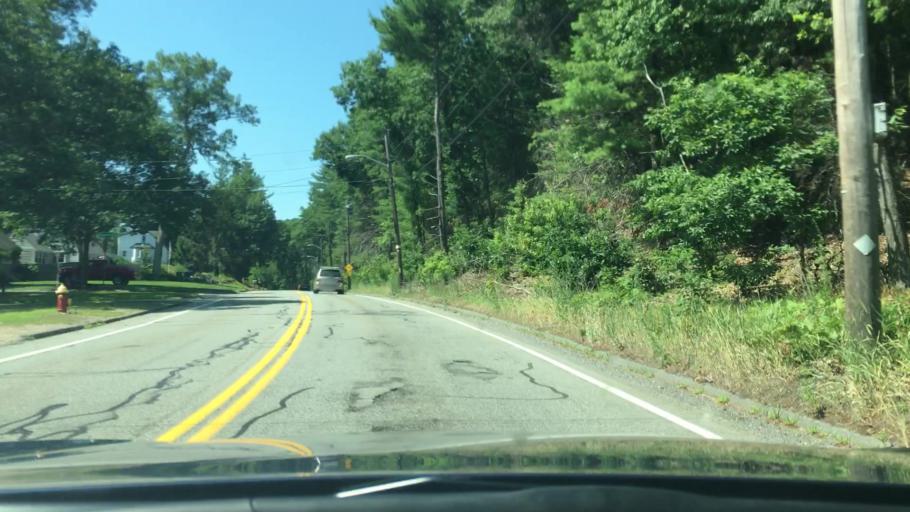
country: US
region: Massachusetts
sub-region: Middlesex County
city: Billerica
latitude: 42.5717
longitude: -71.2952
